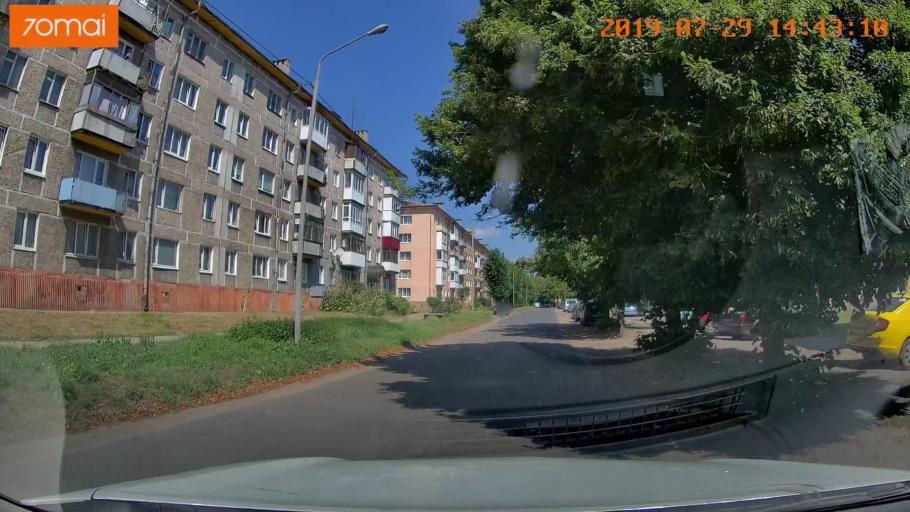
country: RU
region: Kaliningrad
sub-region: Gorod Kaliningrad
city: Baltiysk
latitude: 54.6595
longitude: 19.9053
